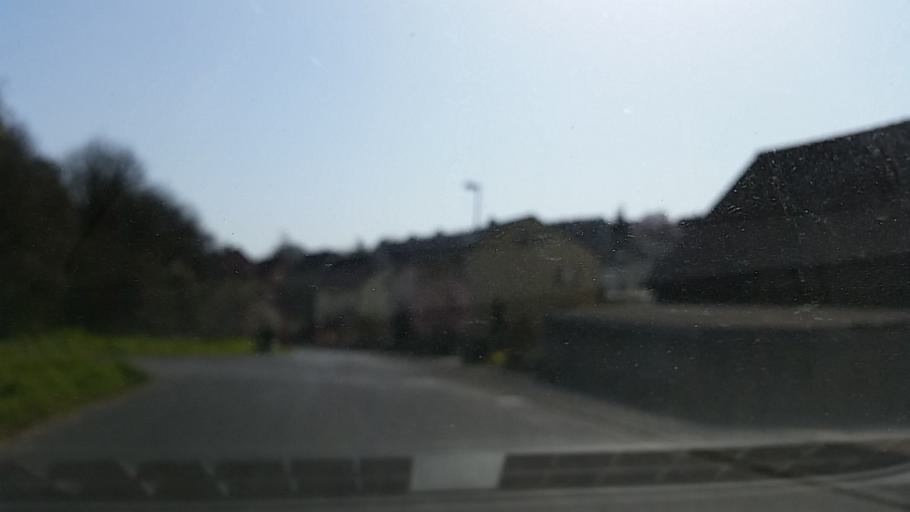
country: DE
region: Bavaria
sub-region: Regierungsbezirk Unterfranken
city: Himmelstadt
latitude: 49.9249
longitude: 9.7944
